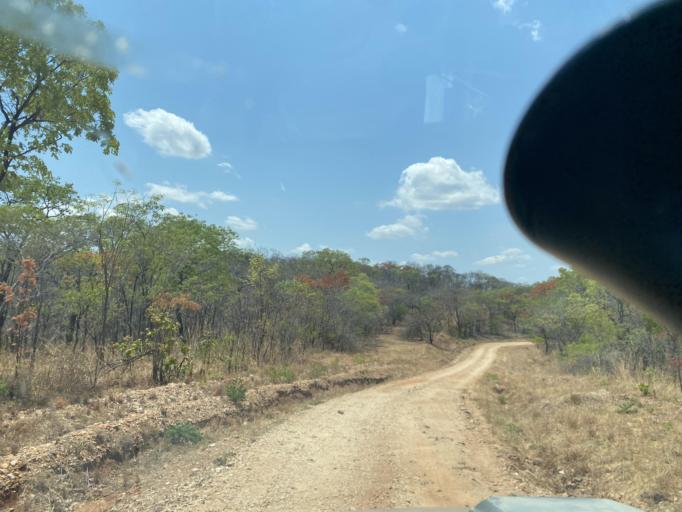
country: ZM
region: Lusaka
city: Luangwa
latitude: -15.0072
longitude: 29.7329
